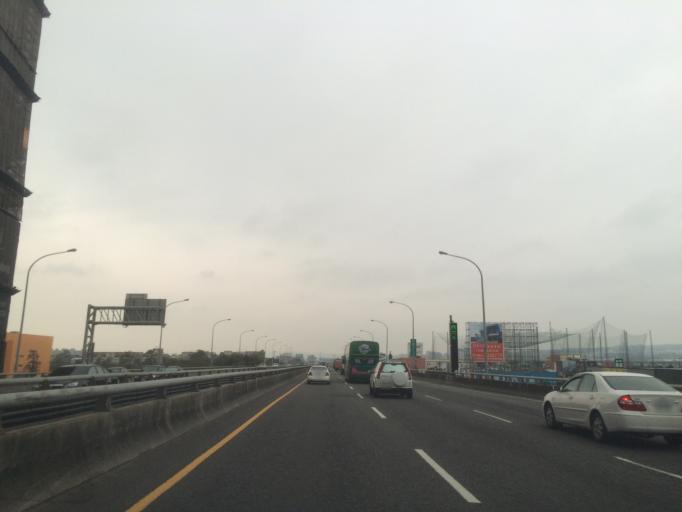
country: TW
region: Taiwan
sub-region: Taichung City
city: Taichung
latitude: 24.1713
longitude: 120.6327
